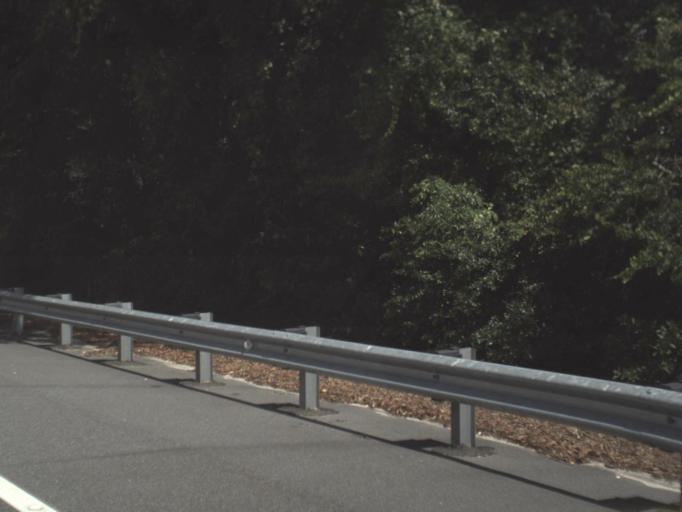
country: US
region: Florida
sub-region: Putnam County
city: Interlachen
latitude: 29.7268
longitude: -81.9320
